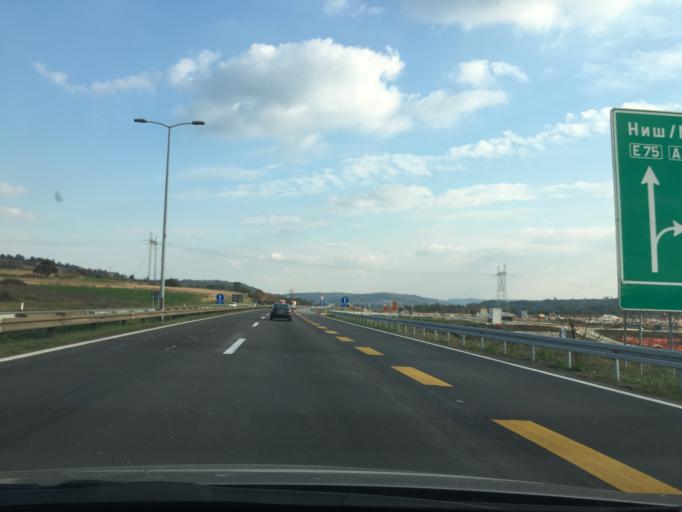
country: RS
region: Central Serbia
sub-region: Belgrade
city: Zvezdara
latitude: 44.7135
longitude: 20.5622
